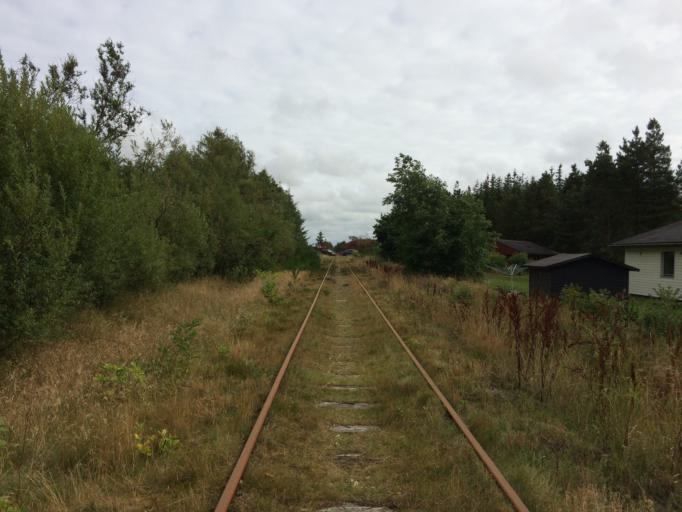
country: DK
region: South Denmark
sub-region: Varde Kommune
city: Oksbol
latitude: 55.7947
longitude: 8.2273
